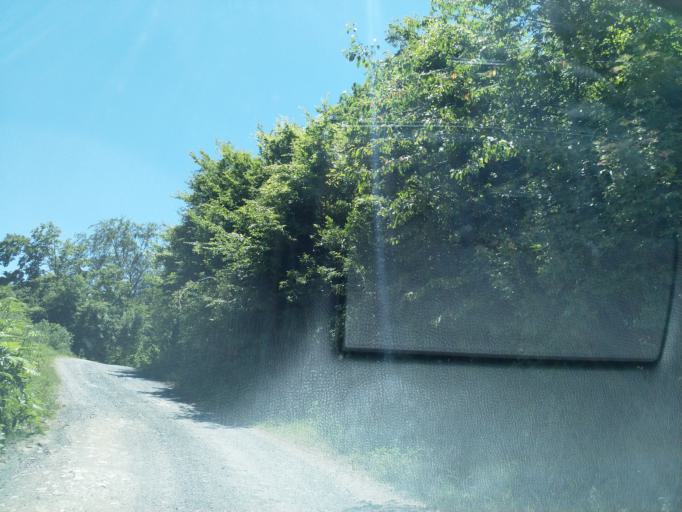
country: XK
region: Mitrovica
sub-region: Komuna e Leposaviqit
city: Leposaviq
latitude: 43.2690
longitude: 20.8727
